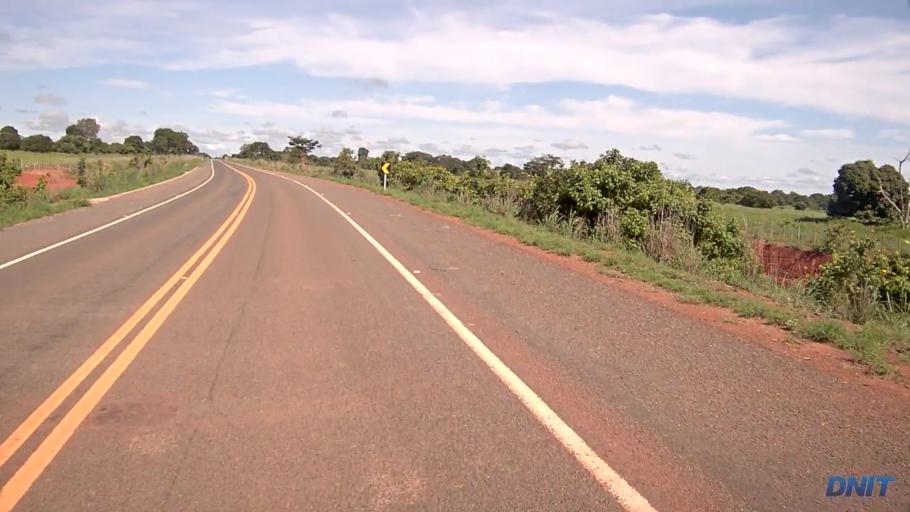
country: BR
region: Goias
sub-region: Sao Miguel Do Araguaia
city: Sao Miguel do Araguaia
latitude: -13.3197
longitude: -50.1605
